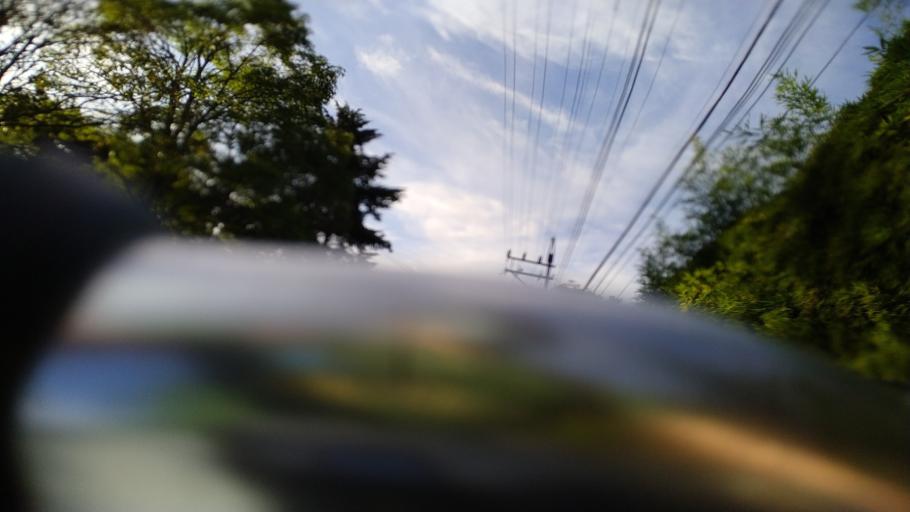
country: CO
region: Antioquia
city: Rionegro
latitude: 6.1383
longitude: -75.3781
